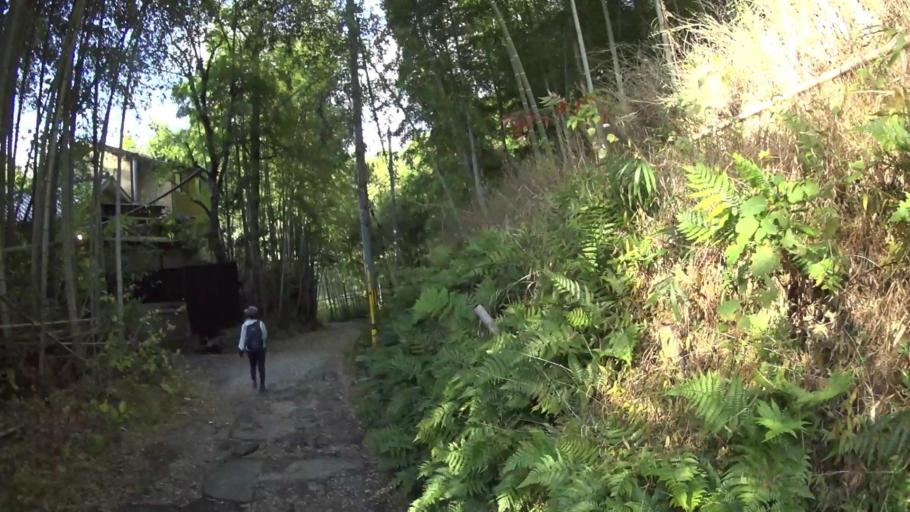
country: JP
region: Kyoto
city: Kyoto
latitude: 34.9614
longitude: 135.7798
